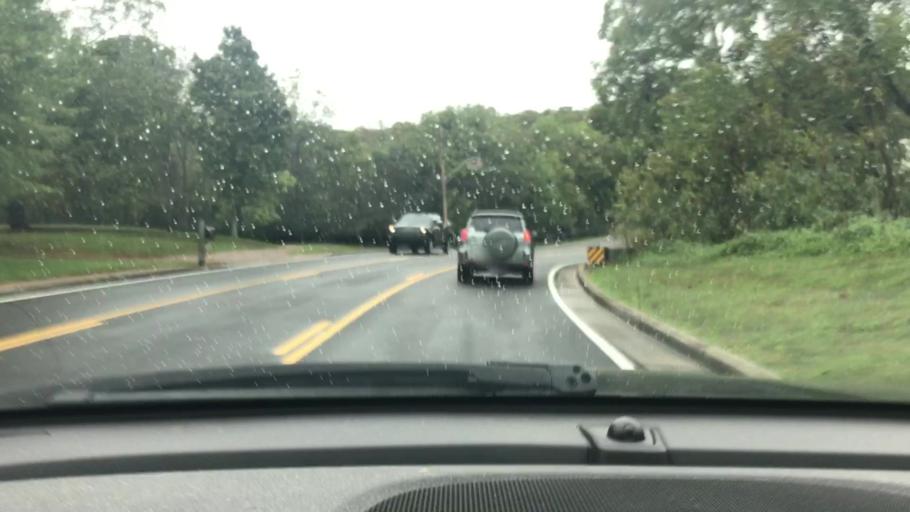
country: US
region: Tennessee
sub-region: Cheatham County
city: Kingston Springs
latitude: 36.0899
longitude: -87.1098
